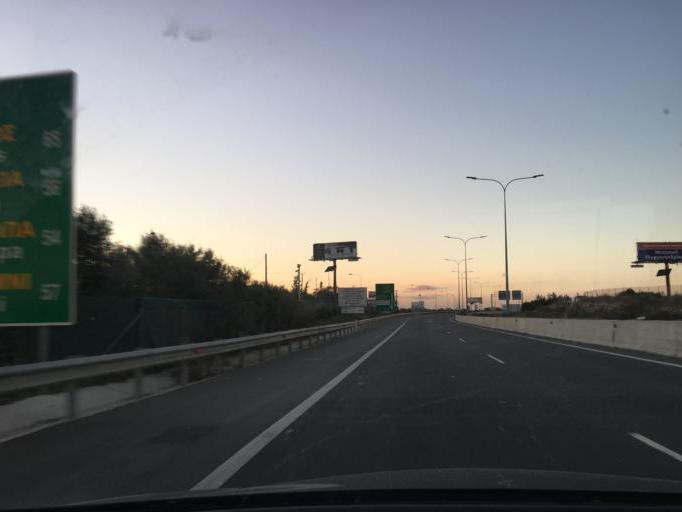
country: CY
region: Larnaka
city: Dhromolaxia
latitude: 34.8790
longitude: 33.5975
